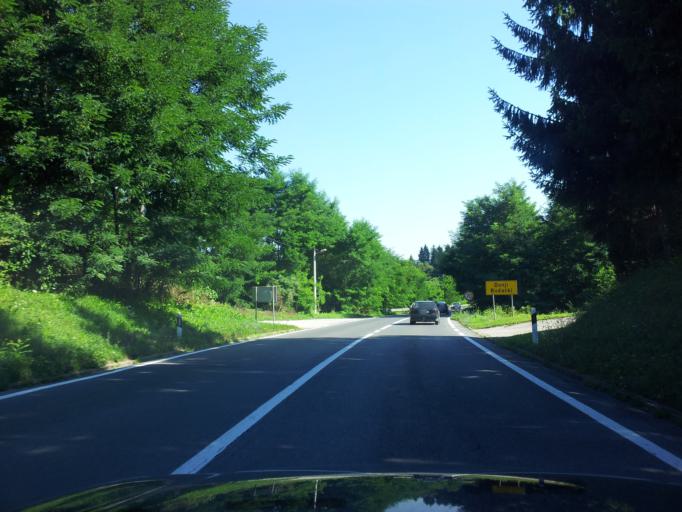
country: HR
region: Karlovacka
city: Vojnic
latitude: 45.3672
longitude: 15.6047
